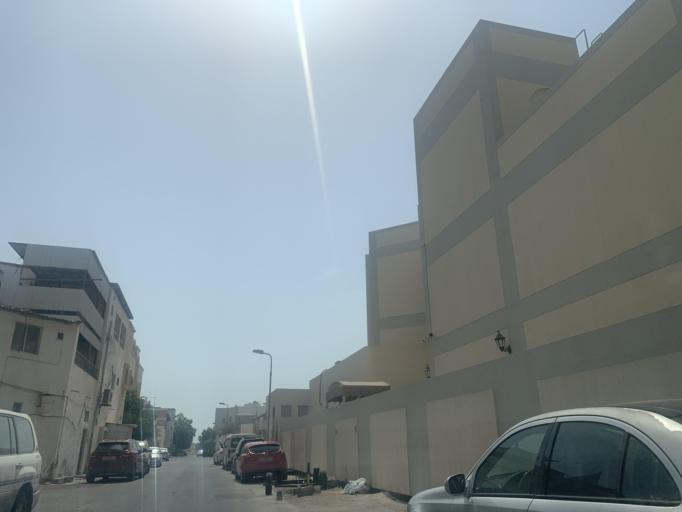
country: BH
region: Manama
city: Jidd Hafs
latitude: 26.2141
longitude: 50.4651
